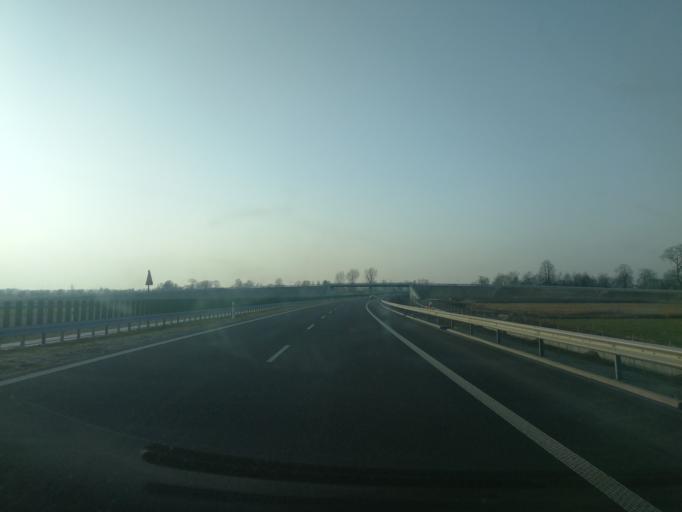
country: PL
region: Pomeranian Voivodeship
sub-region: Powiat nowodworski
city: Nowy Dwor Gdanski
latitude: 54.1748
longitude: 19.1939
